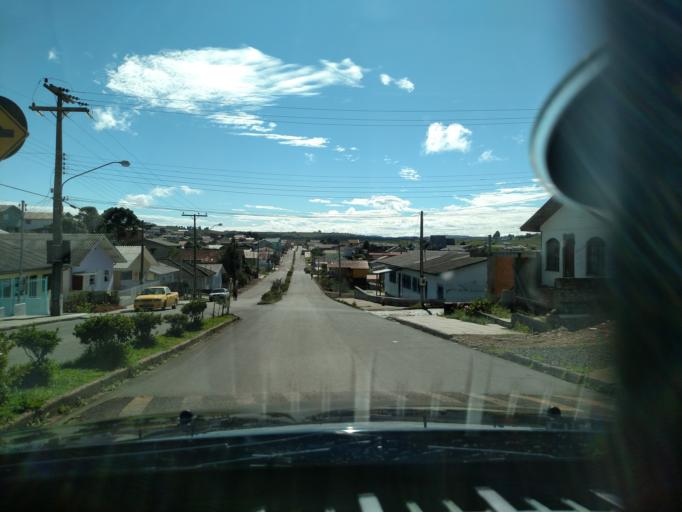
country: BR
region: Santa Catarina
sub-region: Sao Joaquim
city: Sao Joaquim
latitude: -28.2916
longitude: -49.9276
